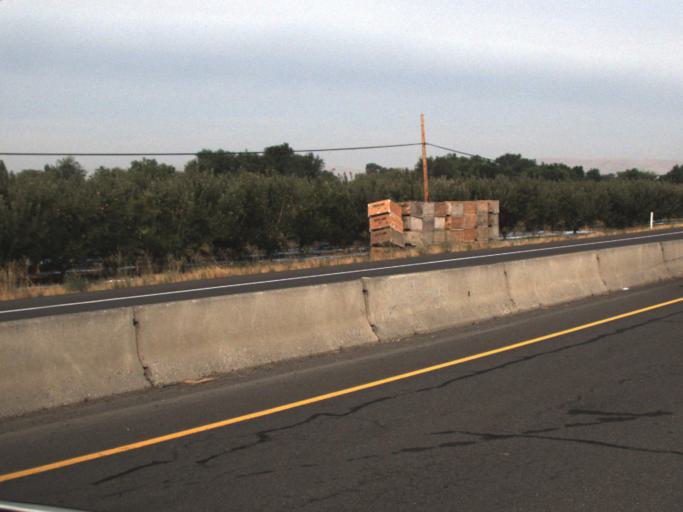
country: US
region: Washington
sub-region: Yakima County
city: Wapato
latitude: 46.4569
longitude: -120.4308
